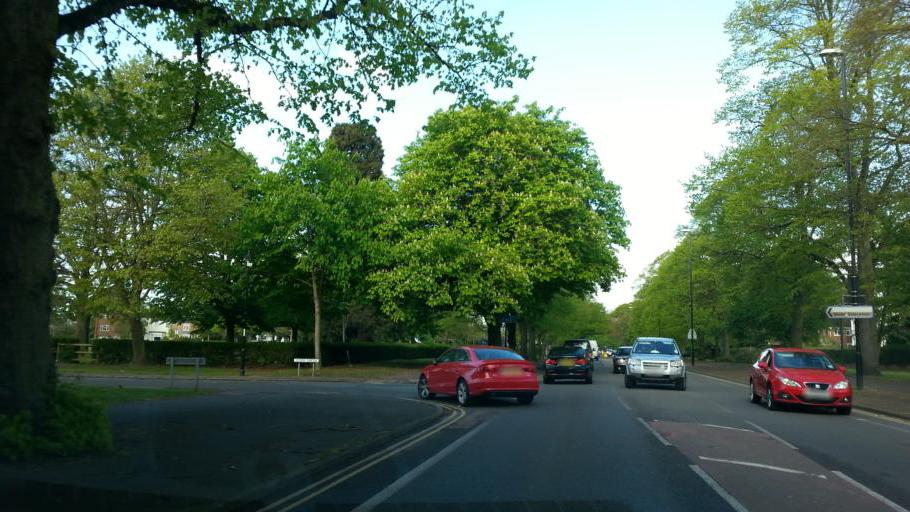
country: GB
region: England
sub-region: Coventry
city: Coventry
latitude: 52.4062
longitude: -1.4804
